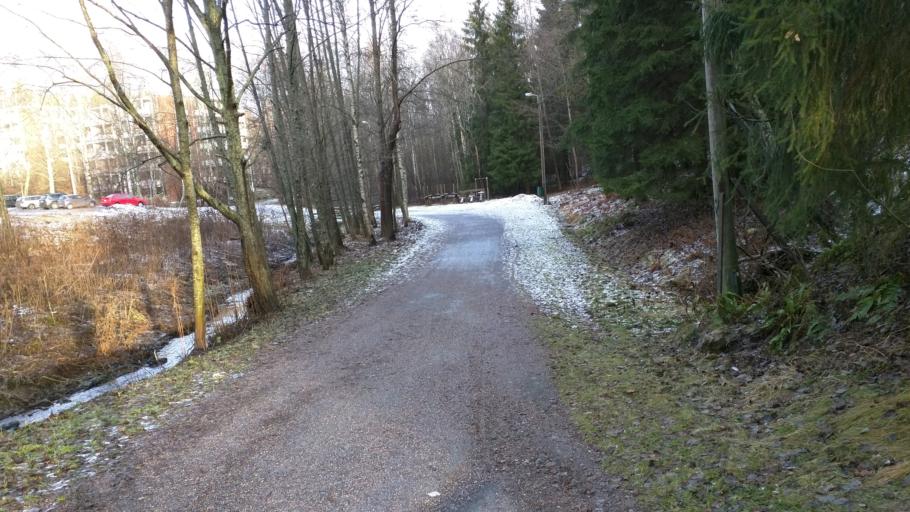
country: FI
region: Uusimaa
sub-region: Helsinki
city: Kilo
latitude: 60.2603
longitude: 24.8083
